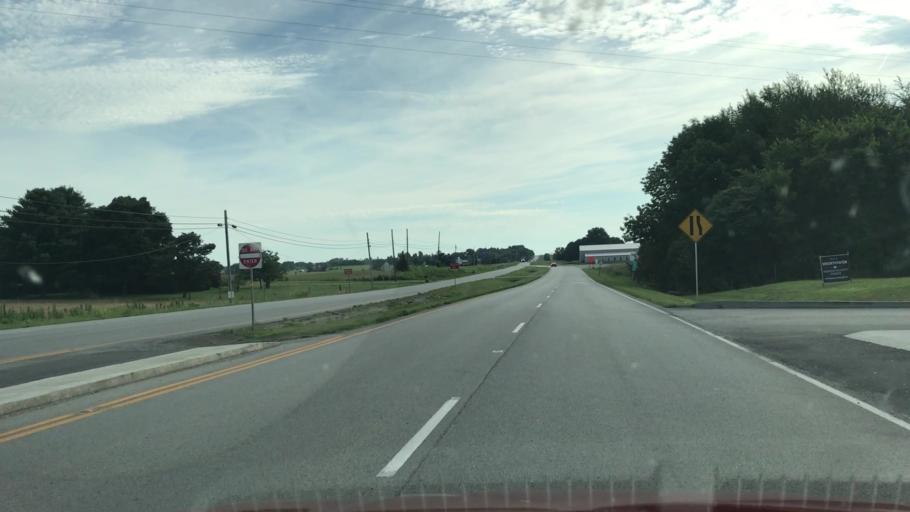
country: US
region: Kentucky
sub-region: Warren County
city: Bowling Green
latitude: 37.0391
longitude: -86.3328
